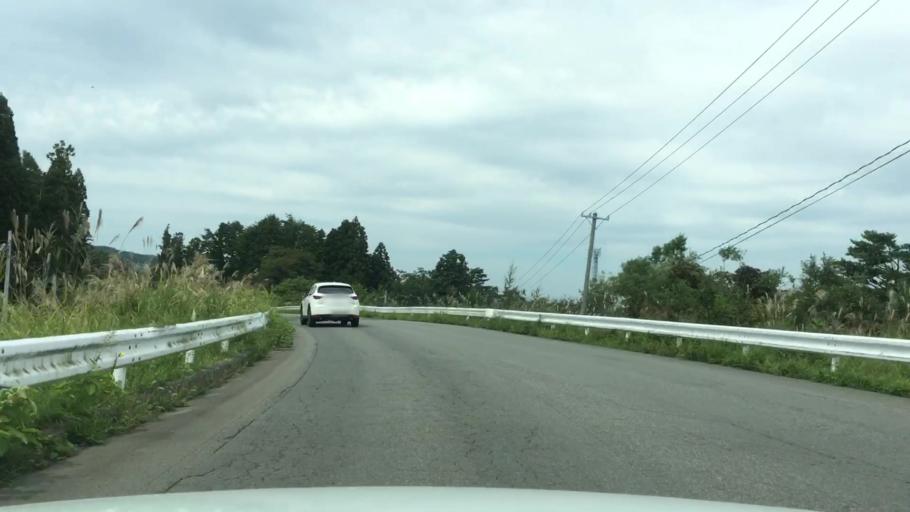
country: JP
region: Aomori
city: Shimokizukuri
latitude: 40.7096
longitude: 140.2766
